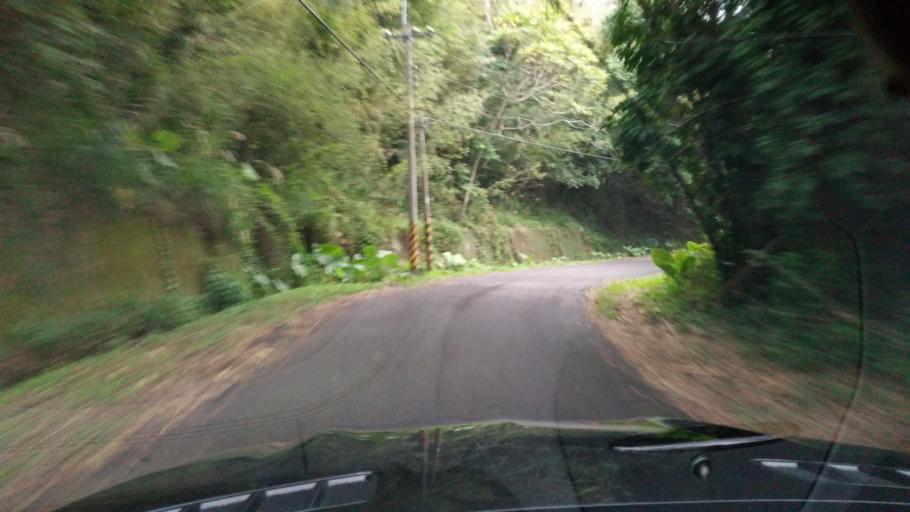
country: TW
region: Taiwan
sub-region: Miaoli
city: Miaoli
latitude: 24.5862
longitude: 120.8980
